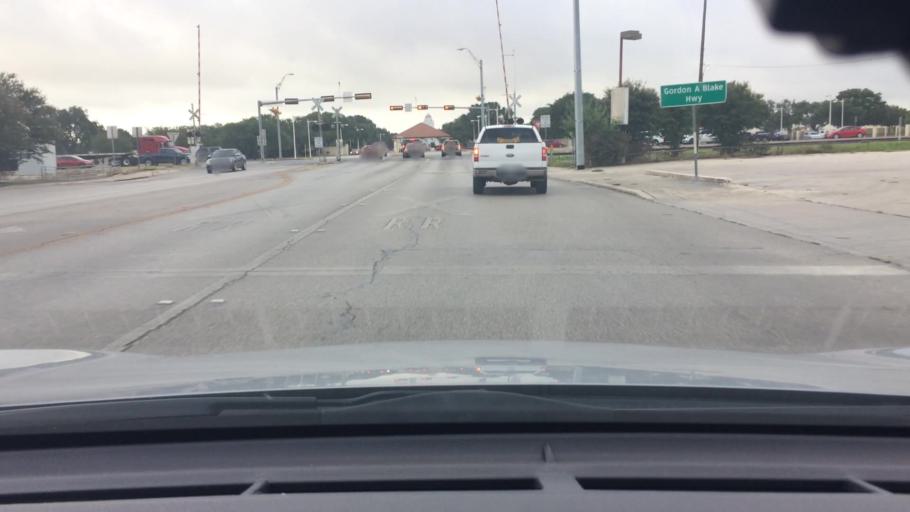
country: US
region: Texas
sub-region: Bexar County
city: Universal City
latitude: 29.5447
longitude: -98.2886
